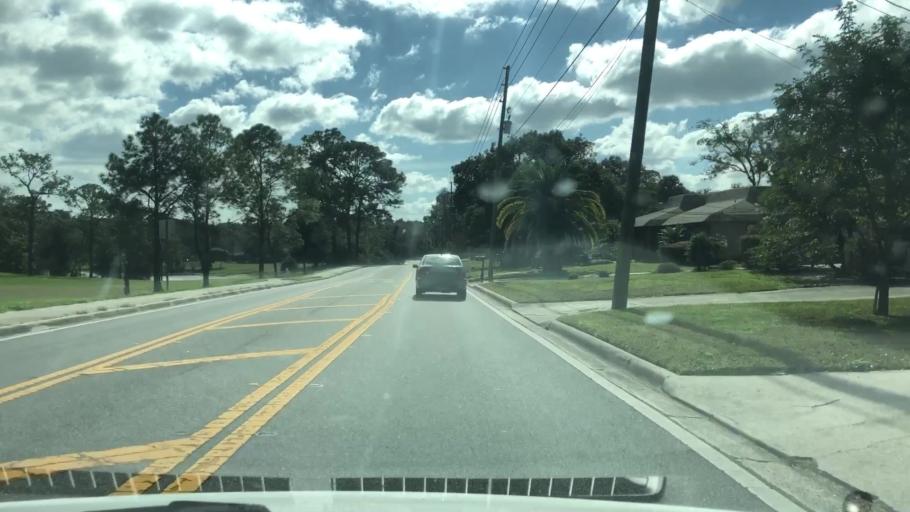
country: US
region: Florida
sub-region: Seminole County
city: Altamonte Springs
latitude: 28.6880
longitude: -81.3862
